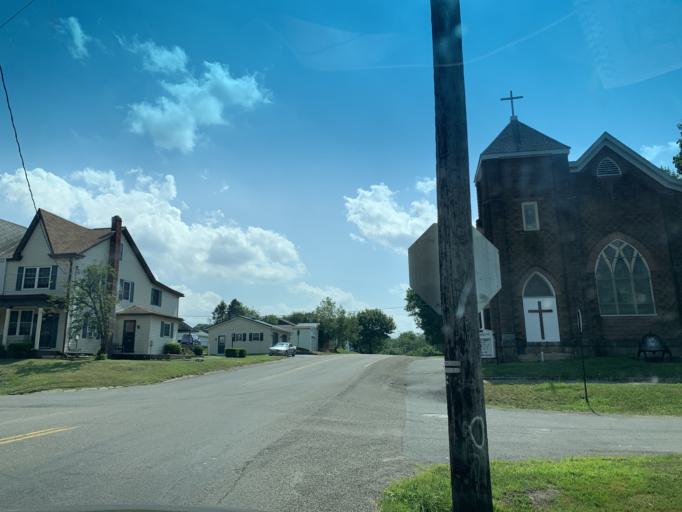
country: US
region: Pennsylvania
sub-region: Schuylkill County
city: Ashland
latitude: 40.8214
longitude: -76.3408
